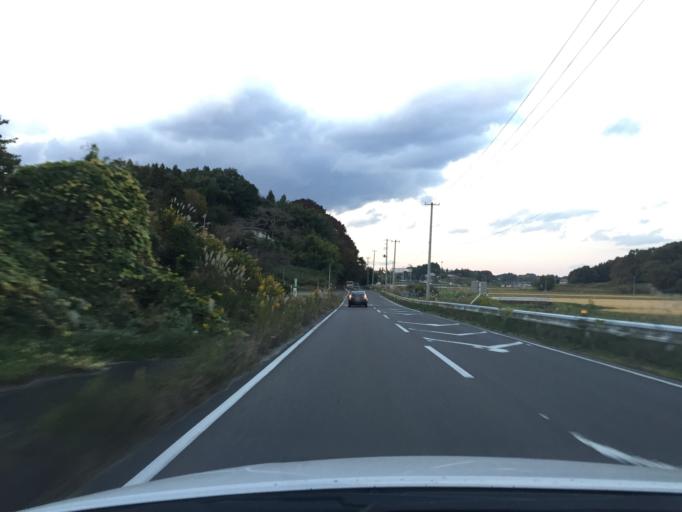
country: JP
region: Fukushima
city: Miharu
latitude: 37.4852
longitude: 140.4532
